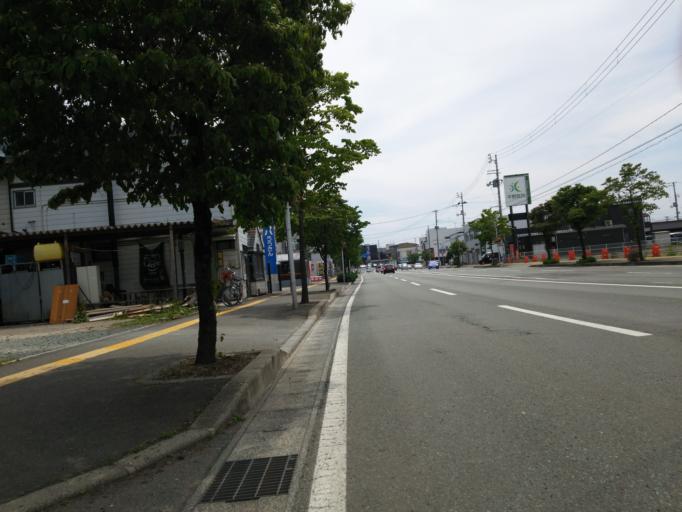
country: JP
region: Iwate
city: Morioka-shi
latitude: 39.7286
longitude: 141.1092
